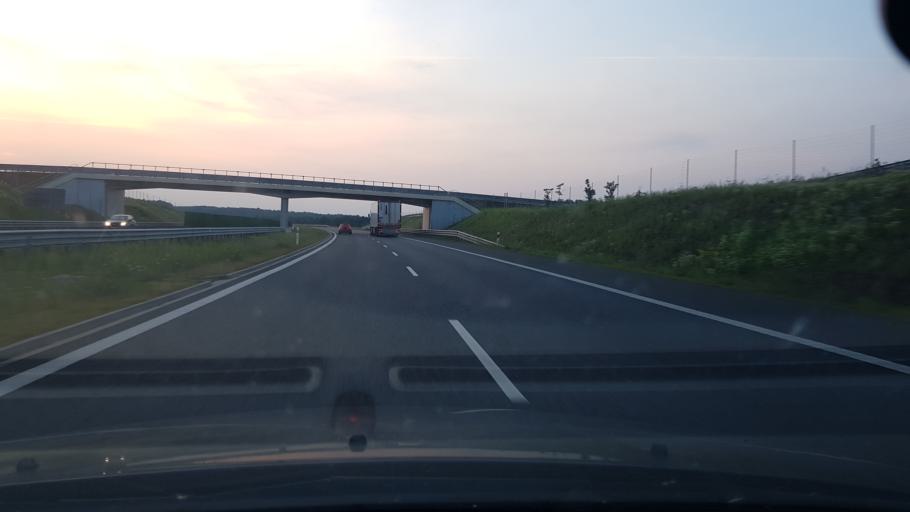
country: PL
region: Warmian-Masurian Voivodeship
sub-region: Powiat nidzicki
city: Nidzica
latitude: 53.4420
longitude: 20.3375
